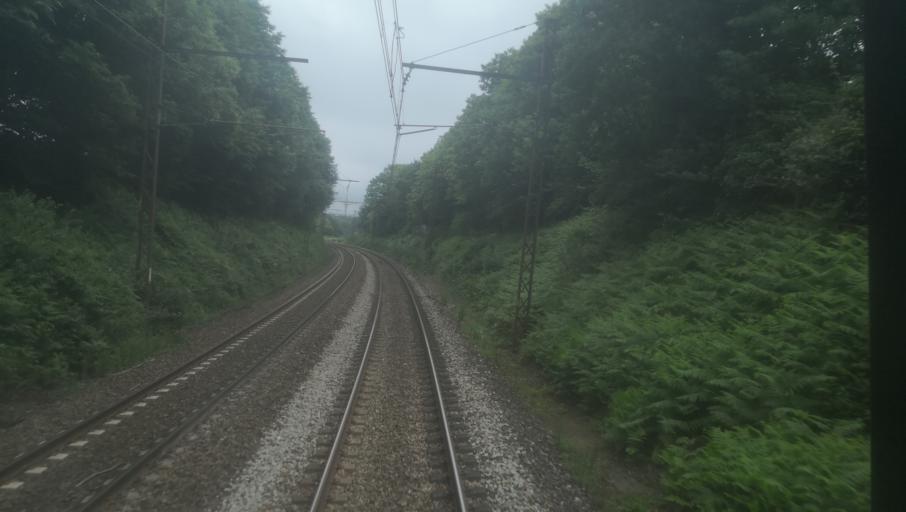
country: FR
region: Limousin
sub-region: Departement de la Creuse
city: Saint-Agnant-de-Versillat
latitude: 46.2875
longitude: 1.4829
